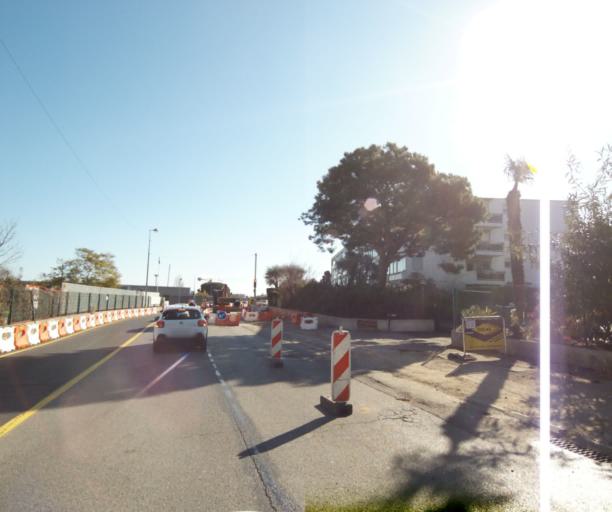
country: FR
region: Provence-Alpes-Cote d'Azur
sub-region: Departement des Alpes-Maritimes
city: Antibes
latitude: 43.5936
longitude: 7.1117
